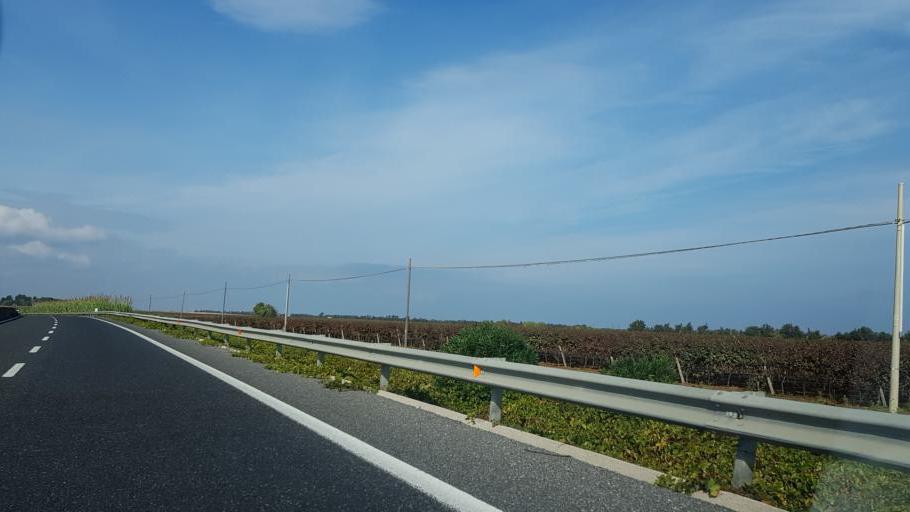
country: IT
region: Apulia
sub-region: Provincia di Brindisi
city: Brindisi
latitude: 40.6664
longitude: 17.8734
